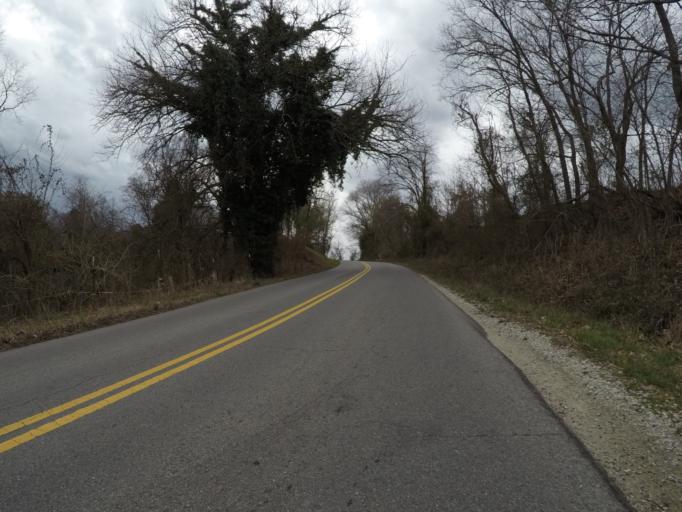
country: US
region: Ohio
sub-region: Lawrence County
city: Burlington
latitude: 38.4327
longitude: -82.5276
